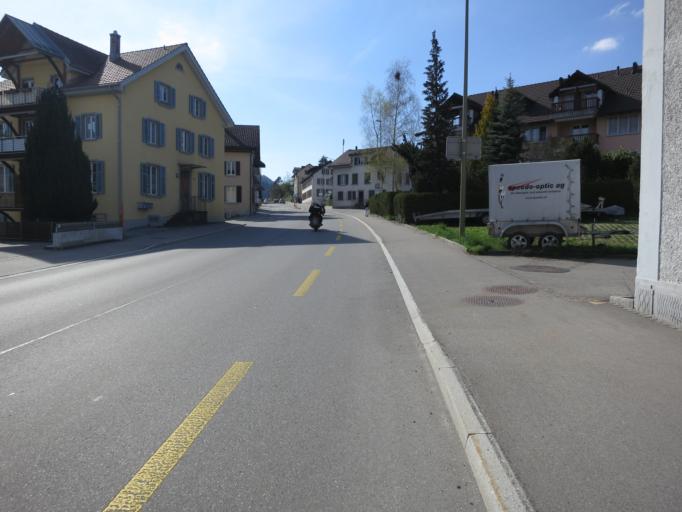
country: CH
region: Zurich
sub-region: Bezirk Hinwil
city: Wald
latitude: 47.2655
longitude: 8.9272
